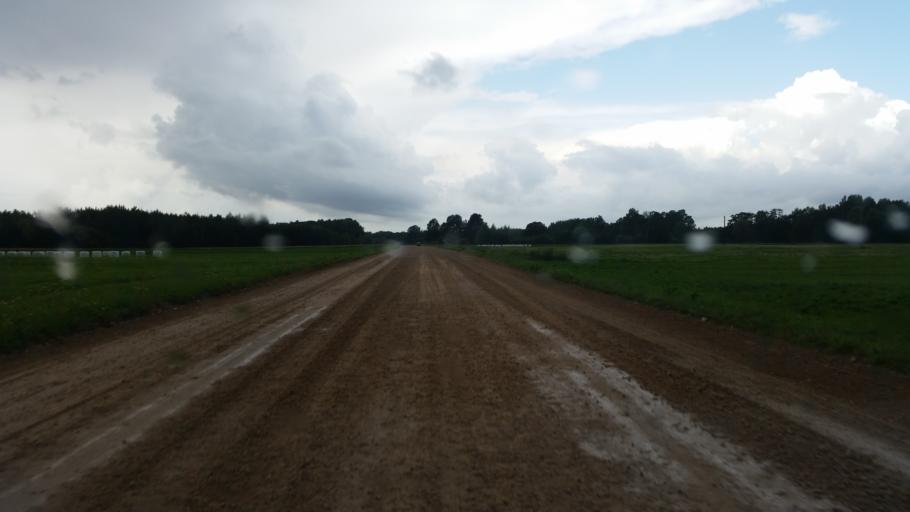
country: LV
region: Vecumnieki
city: Vecumnieki
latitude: 56.4296
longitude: 24.4569
